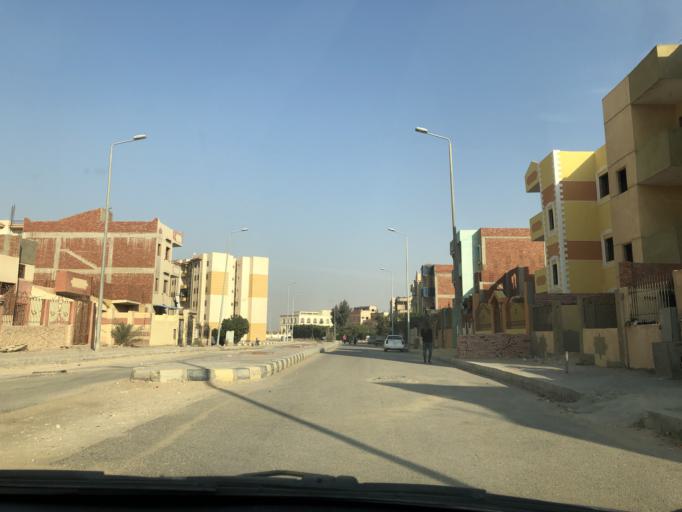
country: EG
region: Al Jizah
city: Madinat Sittah Uktubar
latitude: 29.9059
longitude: 30.9315
